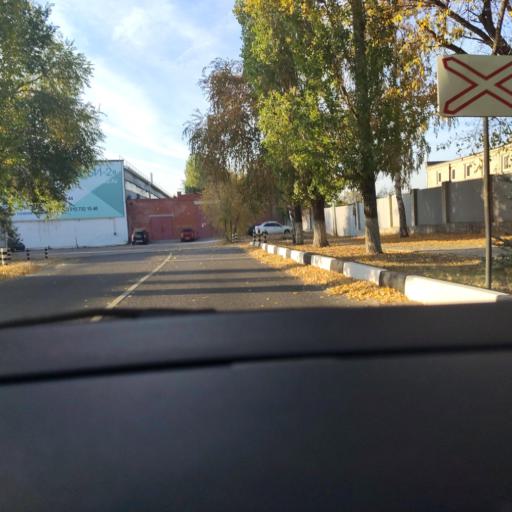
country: RU
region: Voronezj
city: Voronezh
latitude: 51.6608
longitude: 39.1460
